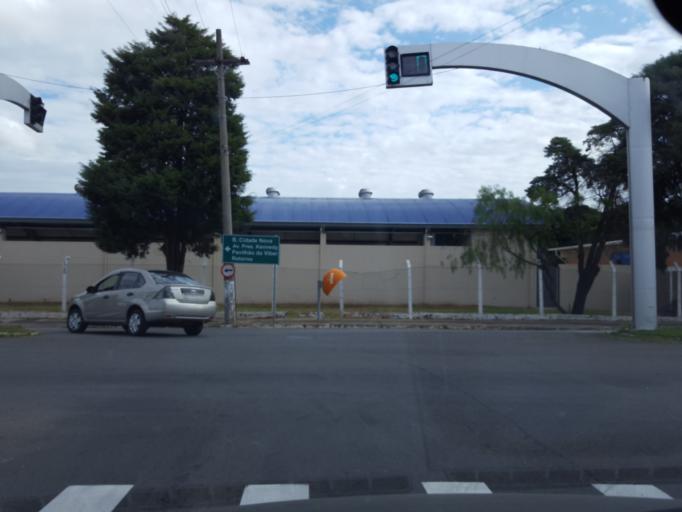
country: BR
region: Sao Paulo
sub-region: Indaiatuba
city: Indaiatuba
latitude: -23.0787
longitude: -47.1991
